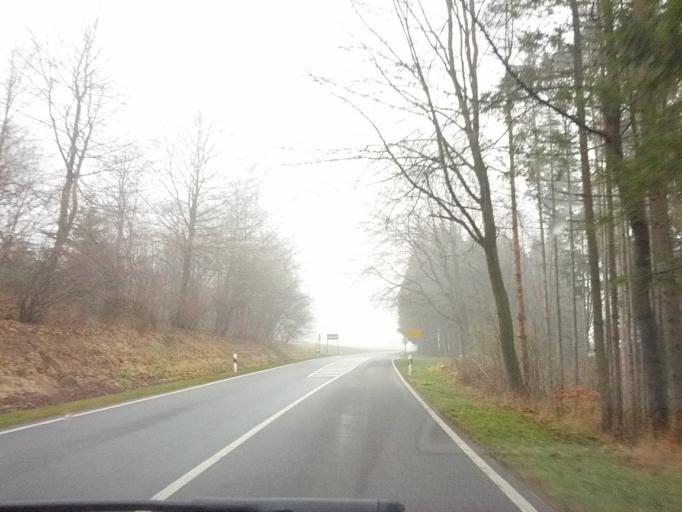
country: DE
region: Baden-Wuerttemberg
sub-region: Tuebingen Region
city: Steinhausen an der Rottum
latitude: 47.9921
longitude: 9.9807
